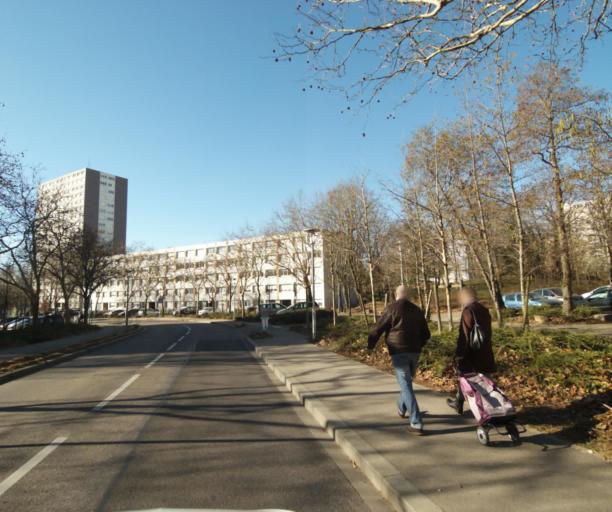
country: FR
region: Lorraine
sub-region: Departement de Meurthe-et-Moselle
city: Laxou
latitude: 48.7017
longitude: 6.1334
